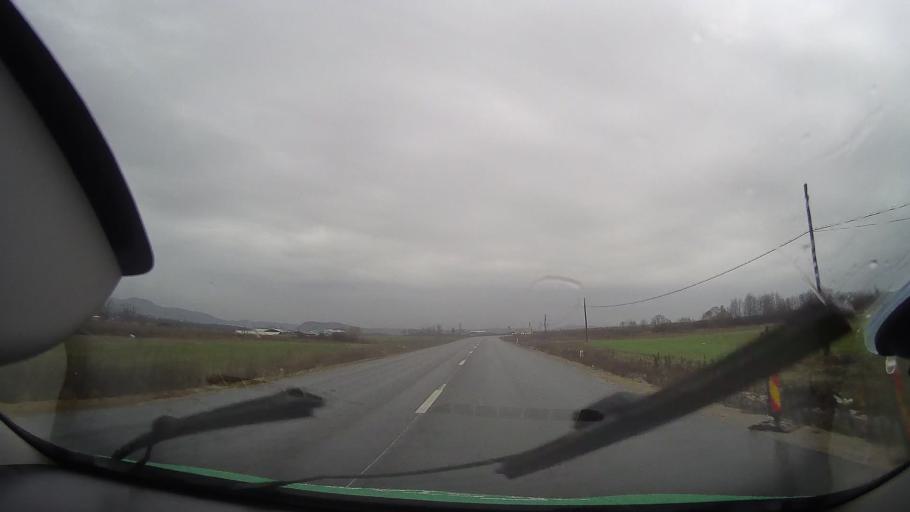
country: RO
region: Bihor
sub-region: Municipiul Beius
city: Beius
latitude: 46.6735
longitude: 22.3268
